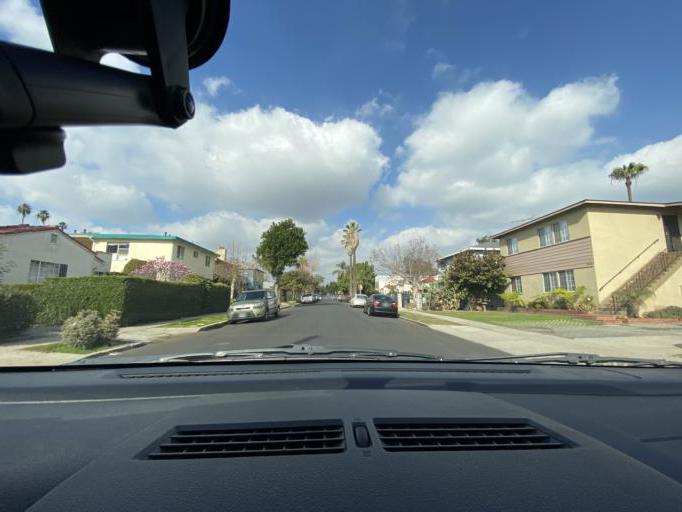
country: US
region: California
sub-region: Los Angeles County
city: Culver City
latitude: 34.0191
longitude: -118.4142
